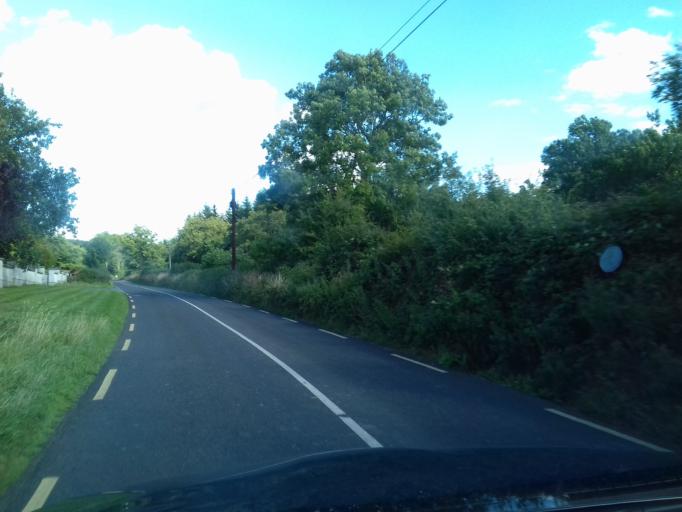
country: IE
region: Leinster
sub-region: Kilkenny
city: Thomastown
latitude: 52.5367
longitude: -7.0997
